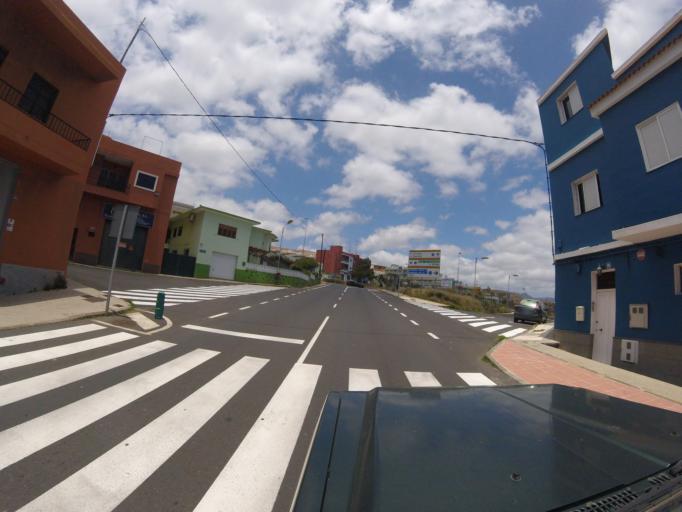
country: ES
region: Canary Islands
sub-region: Provincia de Santa Cruz de Tenerife
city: La Laguna
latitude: 28.4399
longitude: -16.3105
